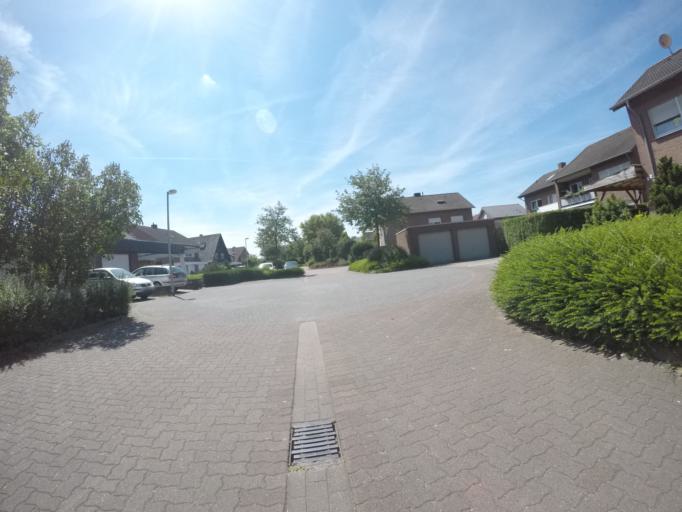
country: DE
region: North Rhine-Westphalia
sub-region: Regierungsbezirk Dusseldorf
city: Bocholt
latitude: 51.8261
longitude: 6.6086
